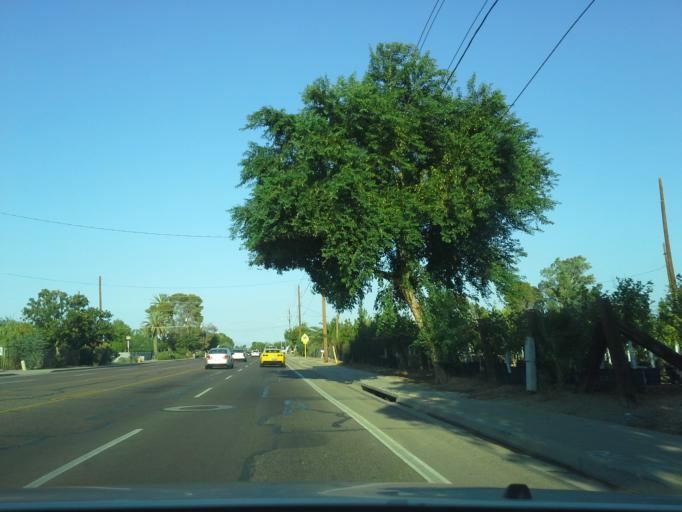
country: US
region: Arizona
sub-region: Maricopa County
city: Guadalupe
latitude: 33.3933
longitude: -112.0239
